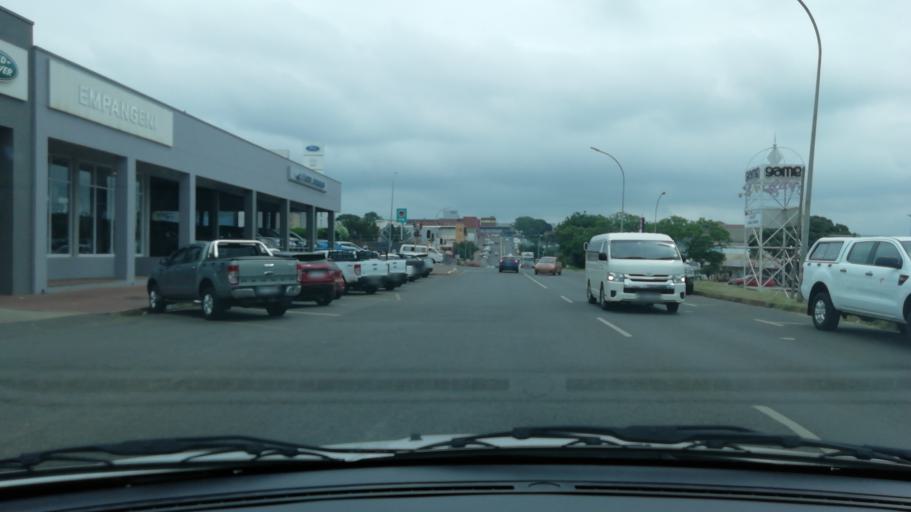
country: ZA
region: KwaZulu-Natal
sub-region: uThungulu District Municipality
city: Empangeni
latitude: -28.7401
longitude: 31.8931
